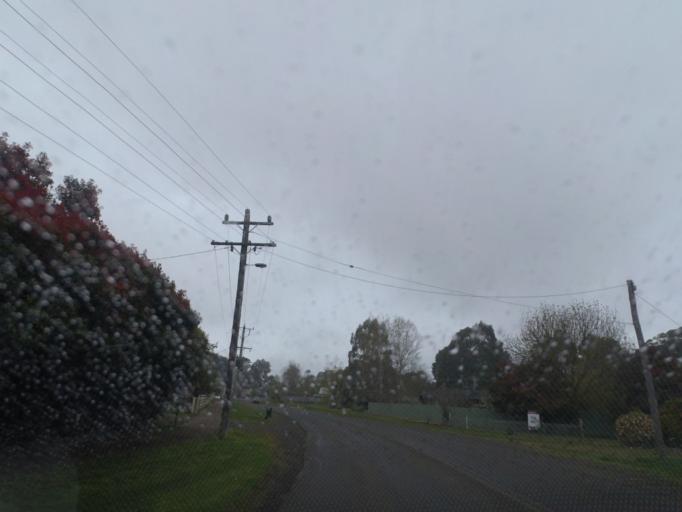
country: AU
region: Victoria
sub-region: Moorabool
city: Bacchus Marsh
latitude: -37.3846
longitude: 144.3159
